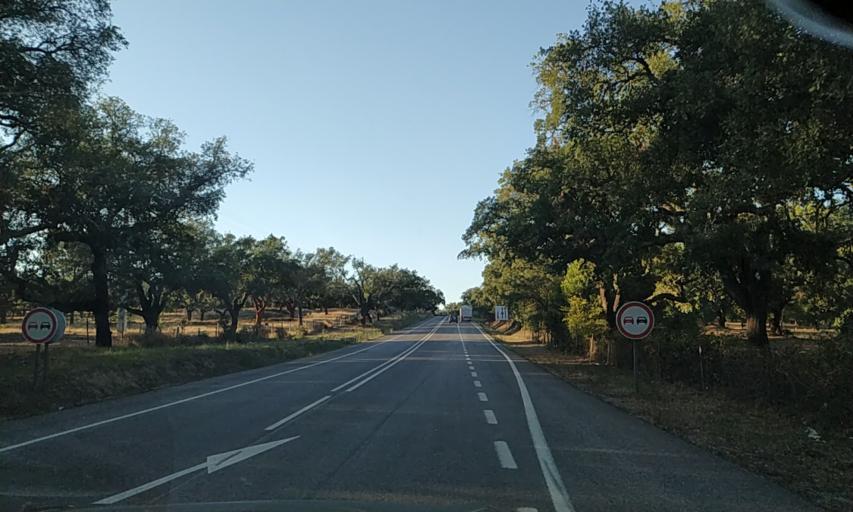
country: PT
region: Setubal
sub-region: Alcacer do Sal
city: Alcacer do Sal
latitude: 38.4985
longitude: -8.6015
